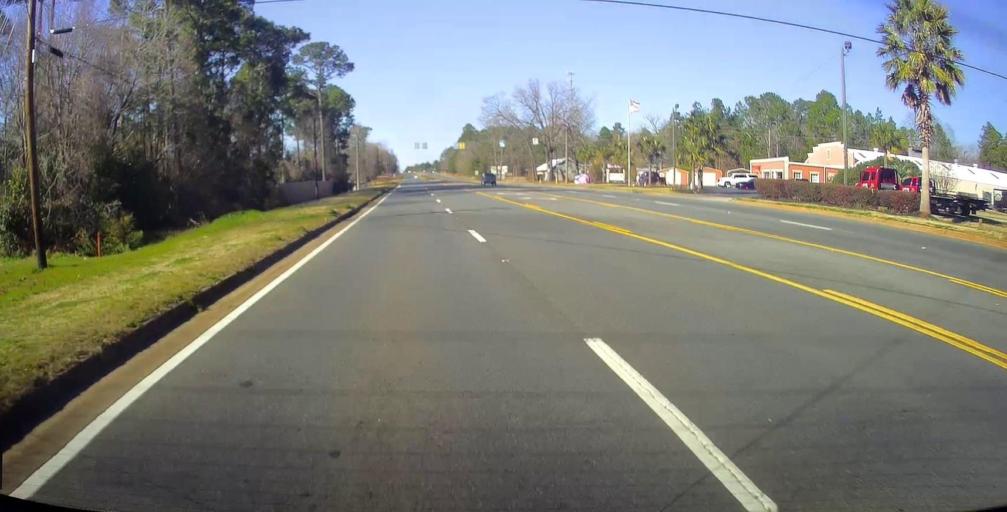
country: US
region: Georgia
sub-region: Sumter County
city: Americus
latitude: 32.0912
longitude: -84.2408
